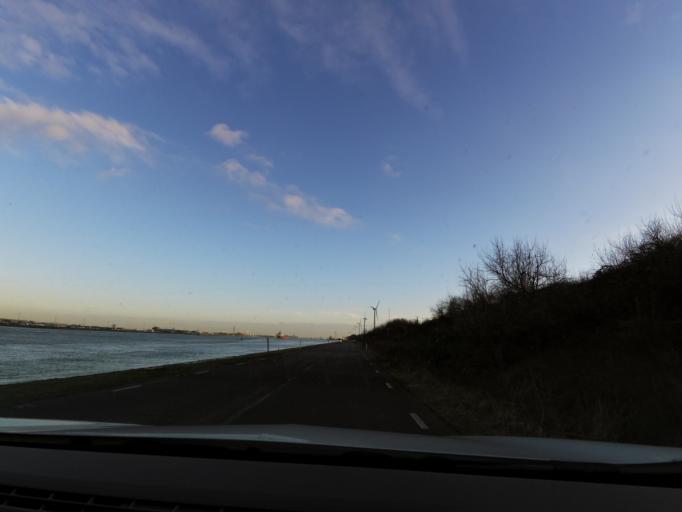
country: NL
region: South Holland
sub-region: Gemeente Rotterdam
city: Hoek van Holland
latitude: 51.9684
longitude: 4.1291
